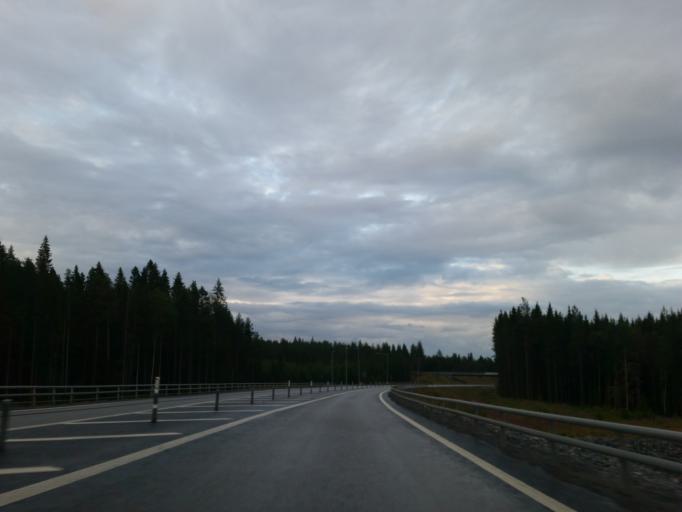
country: SE
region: Vaesterbotten
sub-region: Umea Kommun
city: Umea
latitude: 63.8541
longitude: 20.2783
